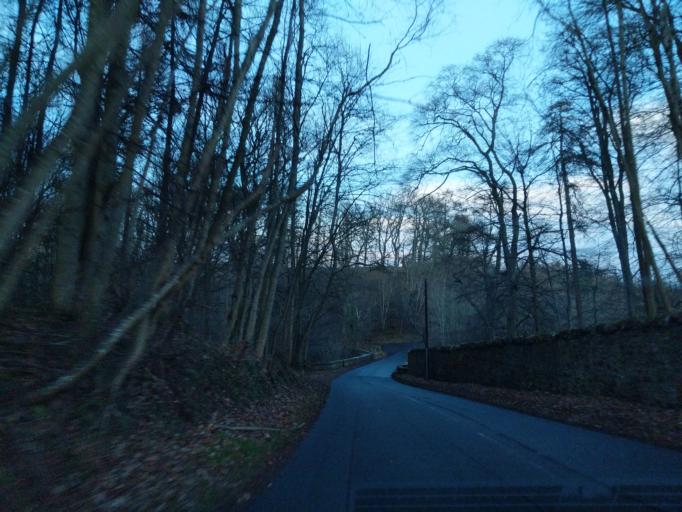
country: GB
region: Scotland
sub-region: Midlothian
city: Gorebridge
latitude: 55.8232
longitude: -3.0868
